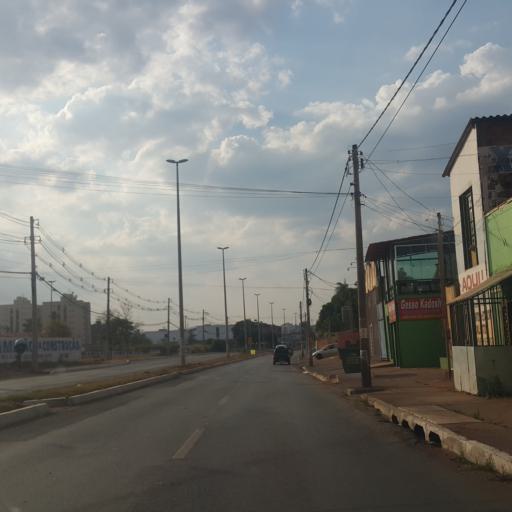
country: BR
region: Federal District
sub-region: Brasilia
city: Brasilia
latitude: -15.8573
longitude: -48.0296
